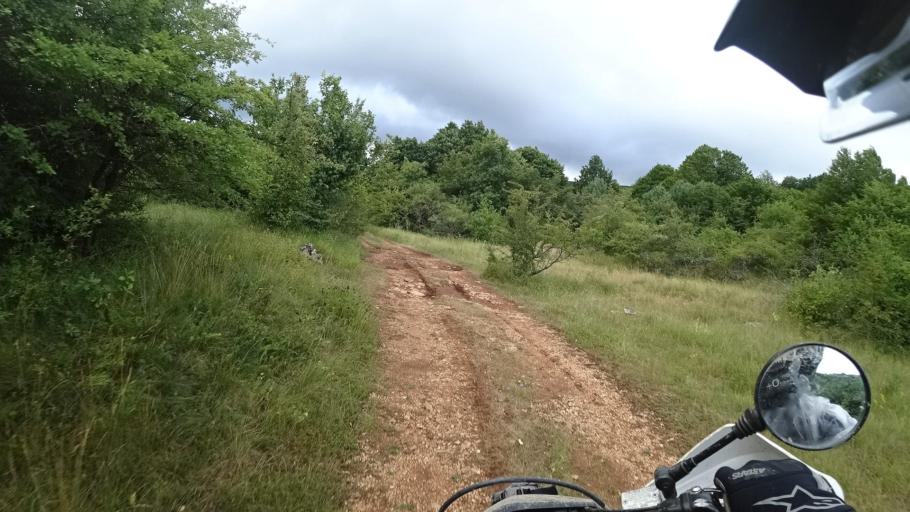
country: HR
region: Licko-Senjska
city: Jezerce
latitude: 44.7623
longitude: 15.4864
